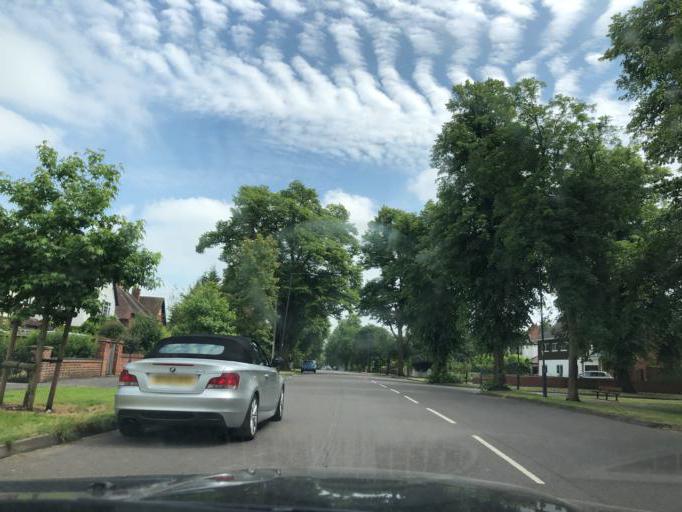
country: GB
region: England
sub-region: Warwickshire
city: Royal Leamington Spa
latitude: 52.2988
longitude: -1.5434
